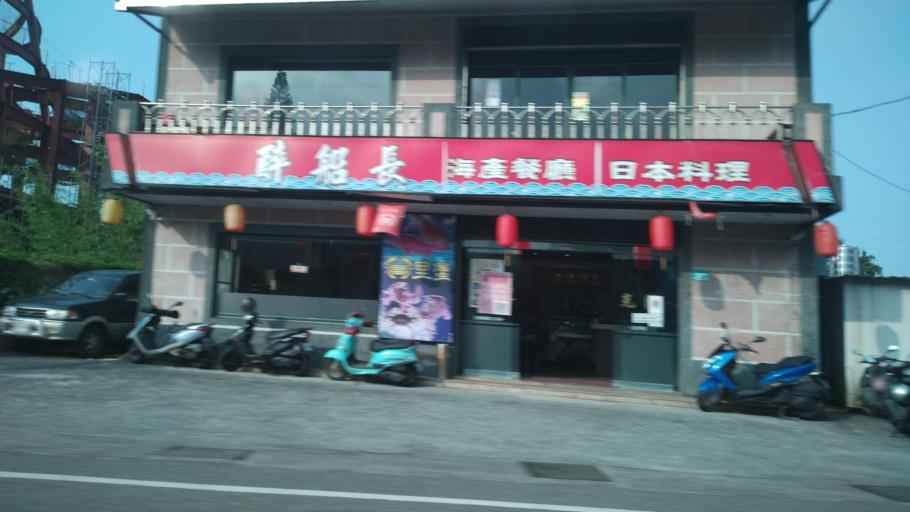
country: TW
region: Taiwan
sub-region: Keelung
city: Keelung
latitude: 25.2176
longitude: 121.6344
